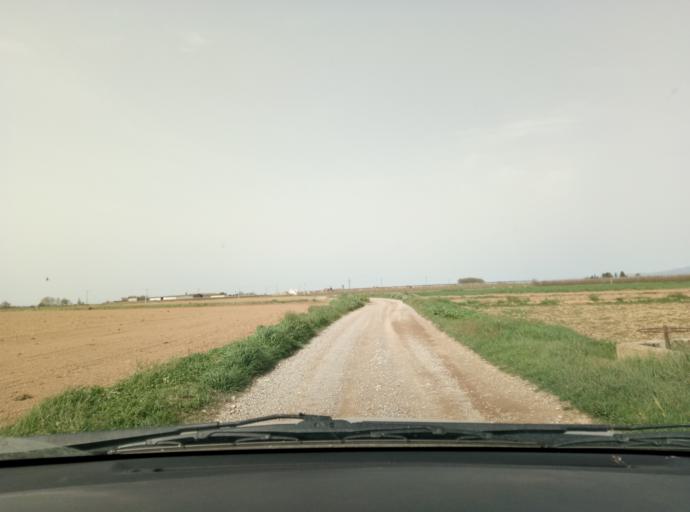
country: ES
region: Catalonia
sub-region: Provincia de Lleida
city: Tornabous
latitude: 41.7143
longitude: 1.0384
